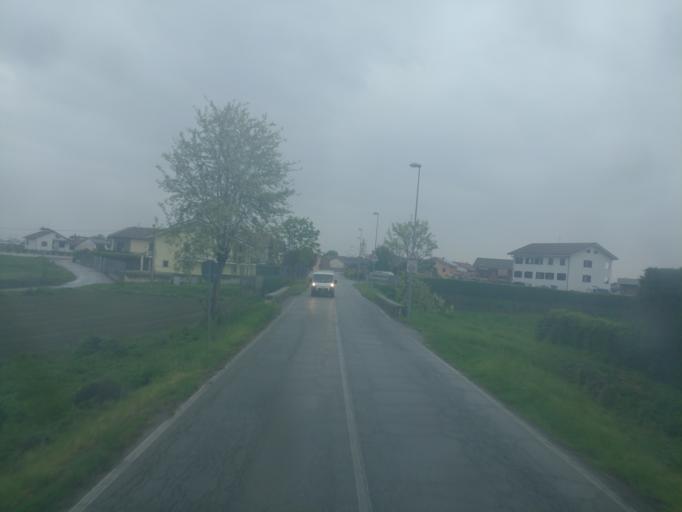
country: IT
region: Piedmont
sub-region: Provincia di Torino
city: Lombriasco
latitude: 44.8376
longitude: 7.6307
